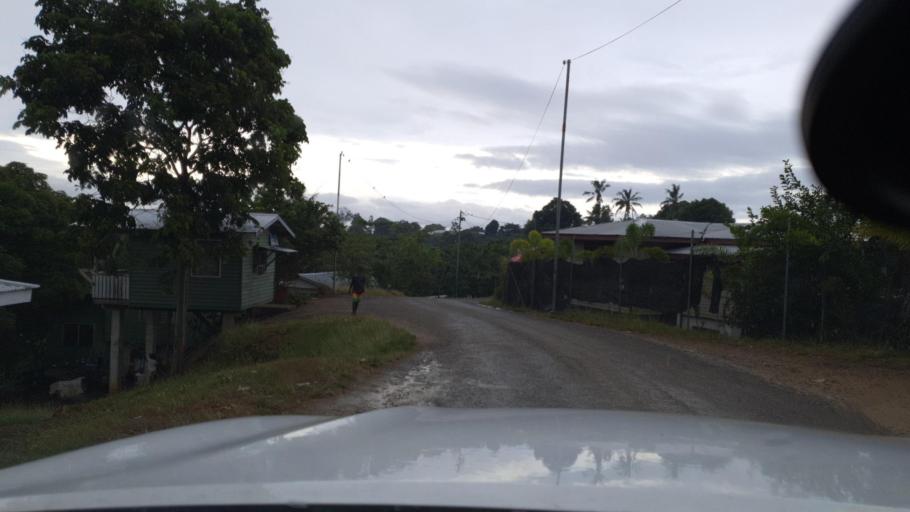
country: SB
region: Guadalcanal
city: Honiara
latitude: -9.4429
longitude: 159.9482
